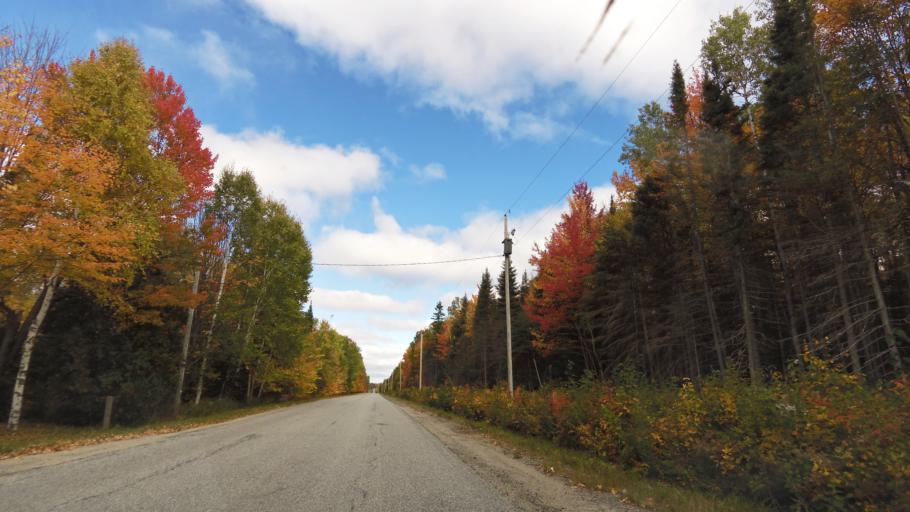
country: CA
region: Ontario
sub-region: Nipissing District
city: North Bay
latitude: 46.3558
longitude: -79.4871
